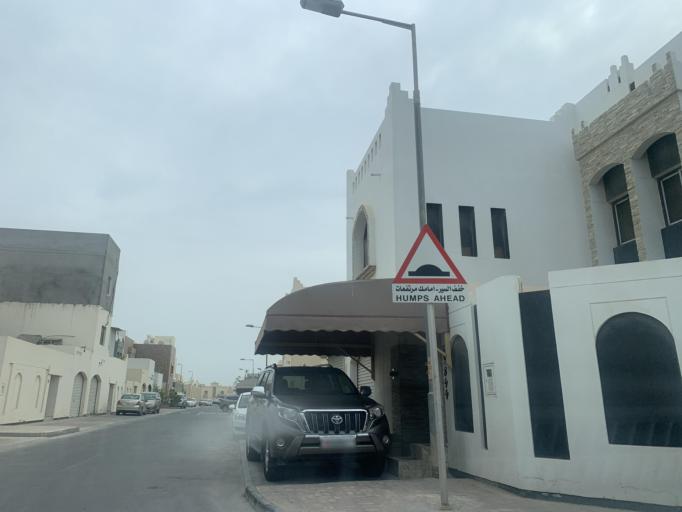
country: BH
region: Muharraq
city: Al Muharraq
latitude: 26.2840
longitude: 50.6416
